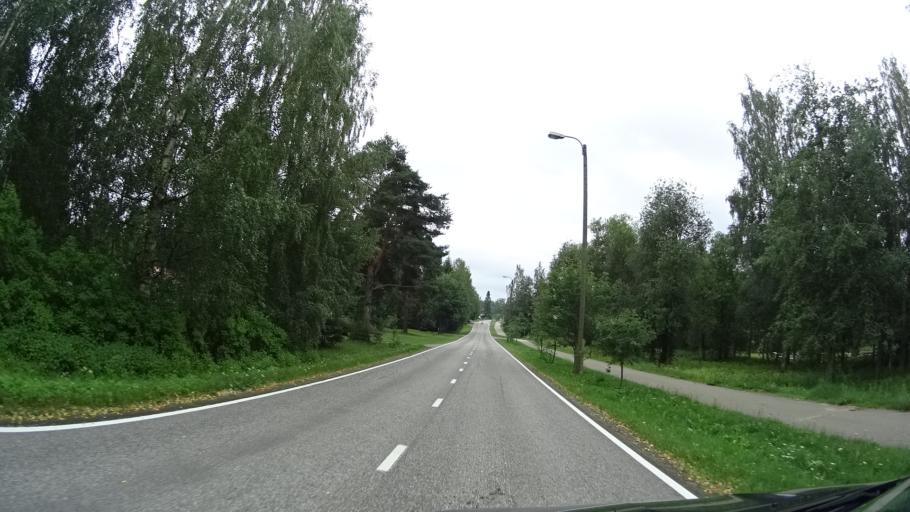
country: FI
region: Southern Savonia
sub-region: Savonlinna
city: Punkaharju
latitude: 61.7501
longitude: 29.3907
